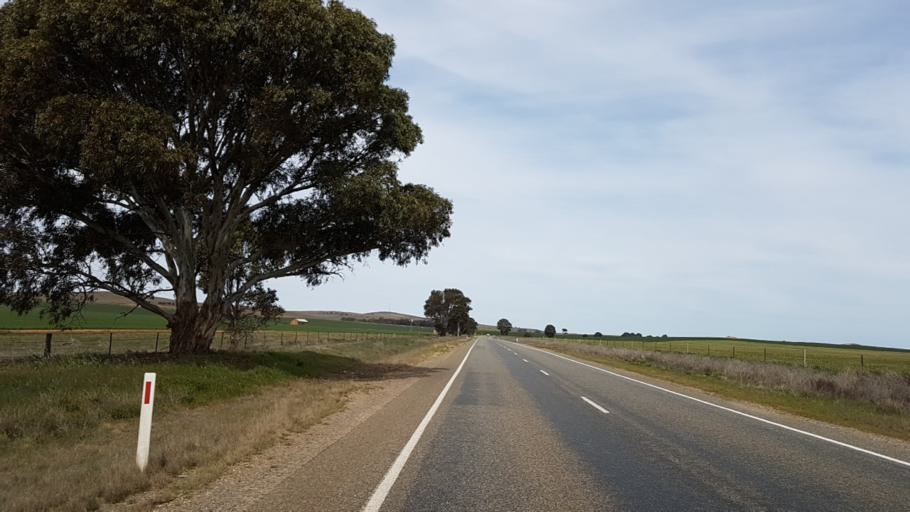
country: AU
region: South Australia
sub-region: Northern Areas
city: Jamestown
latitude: -33.0841
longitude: 138.6180
